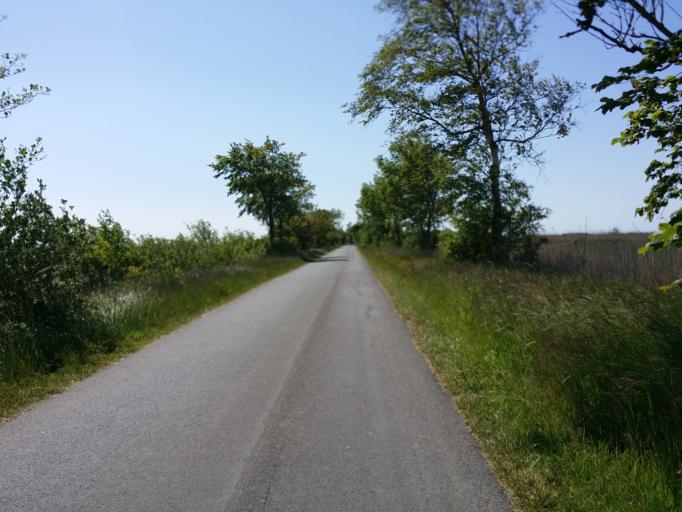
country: DE
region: Lower Saxony
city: Stedesdorf
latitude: 53.6750
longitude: 7.6517
